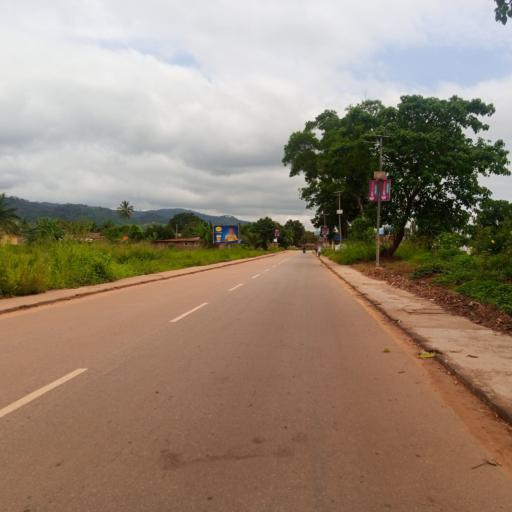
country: SL
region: Eastern Province
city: Kenema
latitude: 7.8564
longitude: -11.2044
